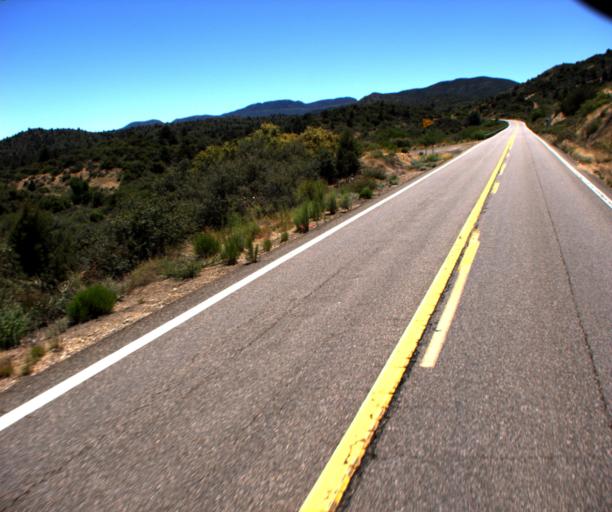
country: US
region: Arizona
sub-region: Gila County
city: Globe
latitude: 33.2936
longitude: -110.7481
